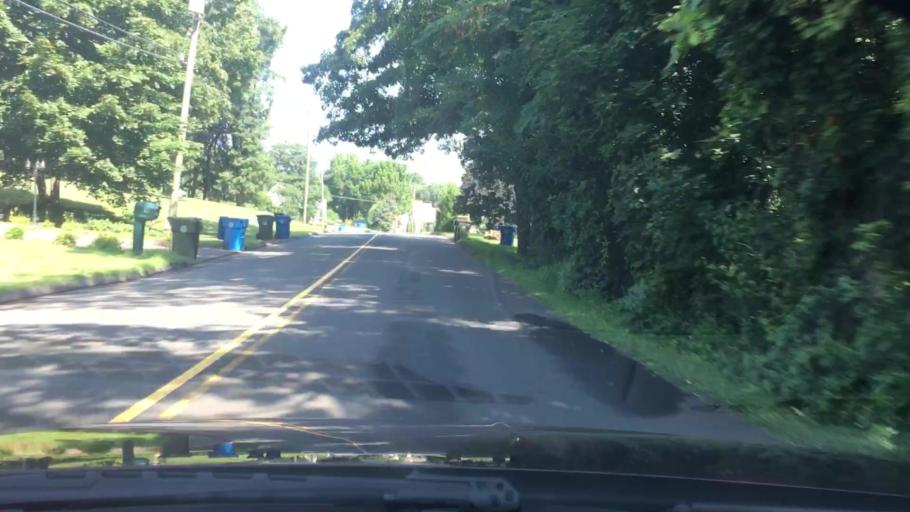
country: US
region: Connecticut
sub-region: Hartford County
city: Kensington
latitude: 41.6029
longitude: -72.7603
